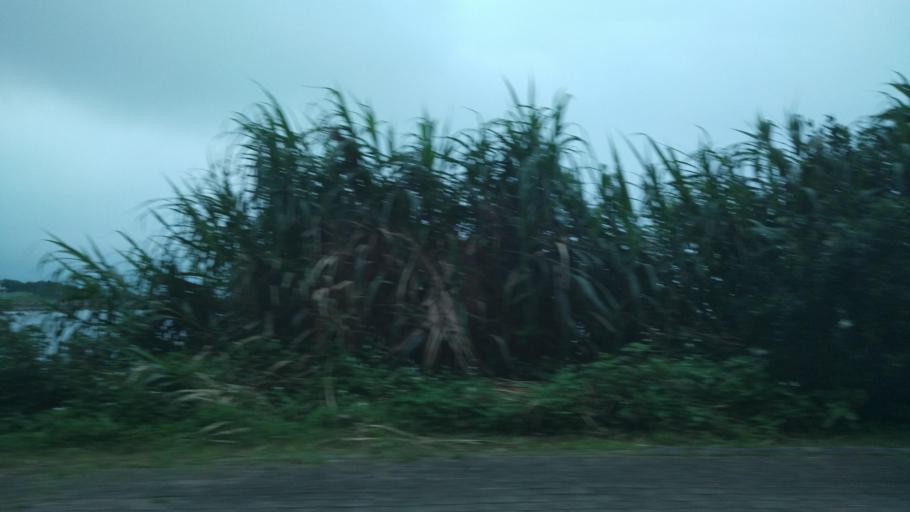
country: TW
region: Taiwan
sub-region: Keelung
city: Keelung
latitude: 25.2026
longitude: 121.6804
